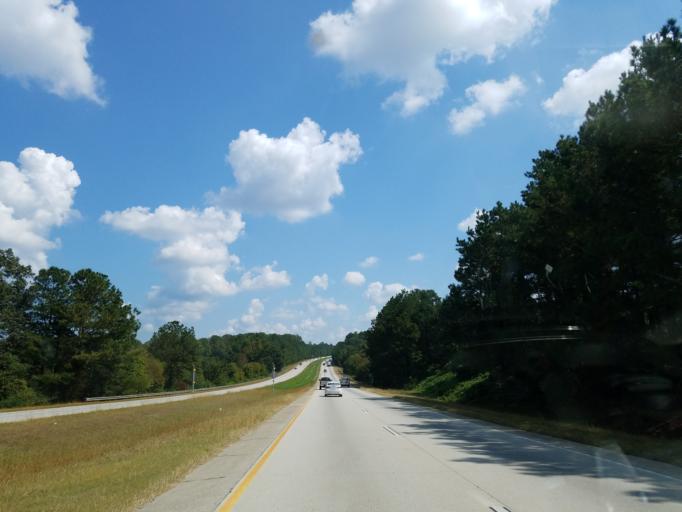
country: US
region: Georgia
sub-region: Barrow County
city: Auburn
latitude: 33.9673
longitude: -83.8176
